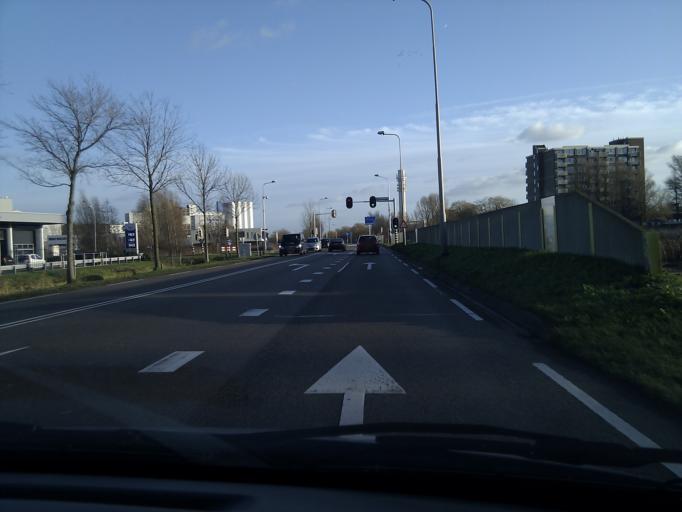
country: NL
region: North Holland
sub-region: Gemeente Zaanstad
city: Zaanstad
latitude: 52.5033
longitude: 4.7824
